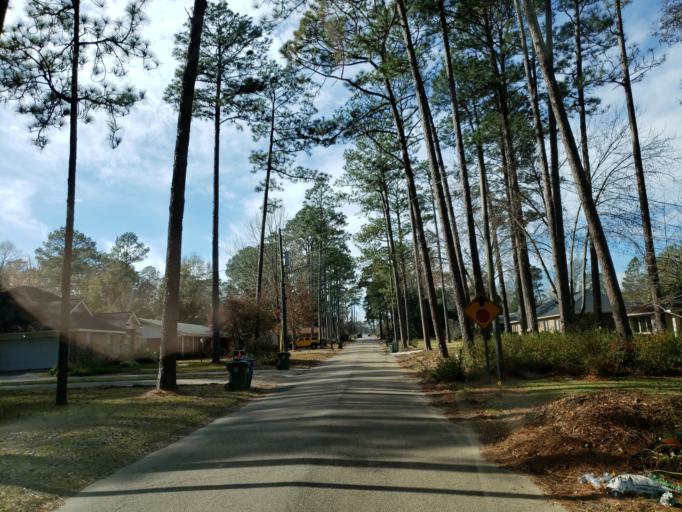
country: US
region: Mississippi
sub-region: Forrest County
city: Hattiesburg
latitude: 31.3121
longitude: -89.3255
